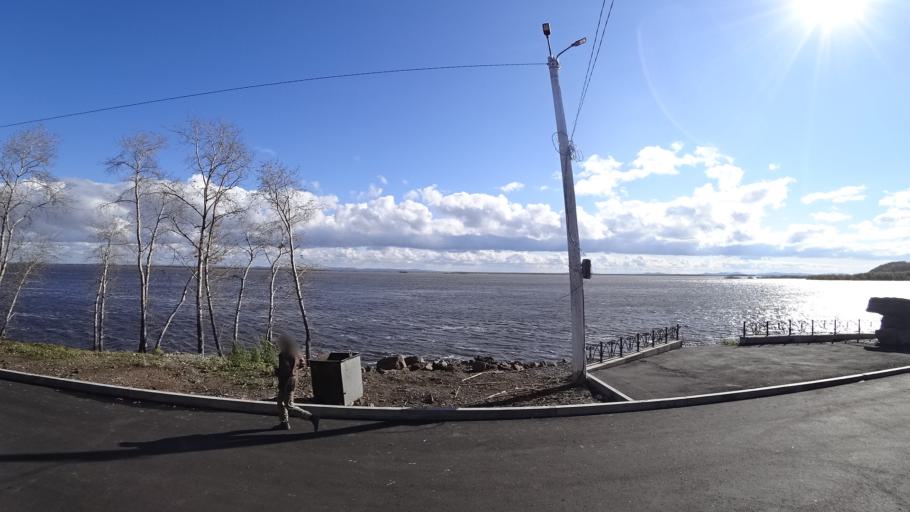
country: RU
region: Khabarovsk Krai
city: Amursk
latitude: 50.2145
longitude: 136.9060
